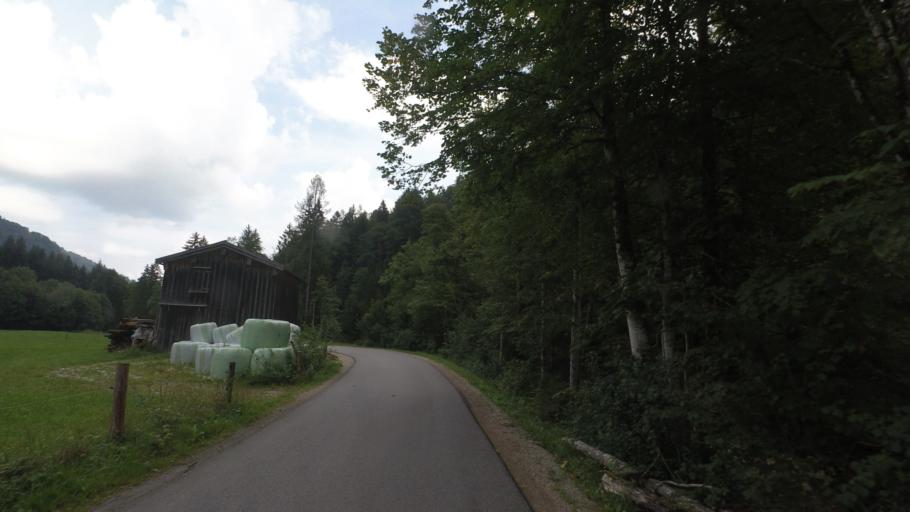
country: DE
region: Bavaria
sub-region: Upper Bavaria
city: Ruhpolding
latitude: 47.7331
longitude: 12.5971
